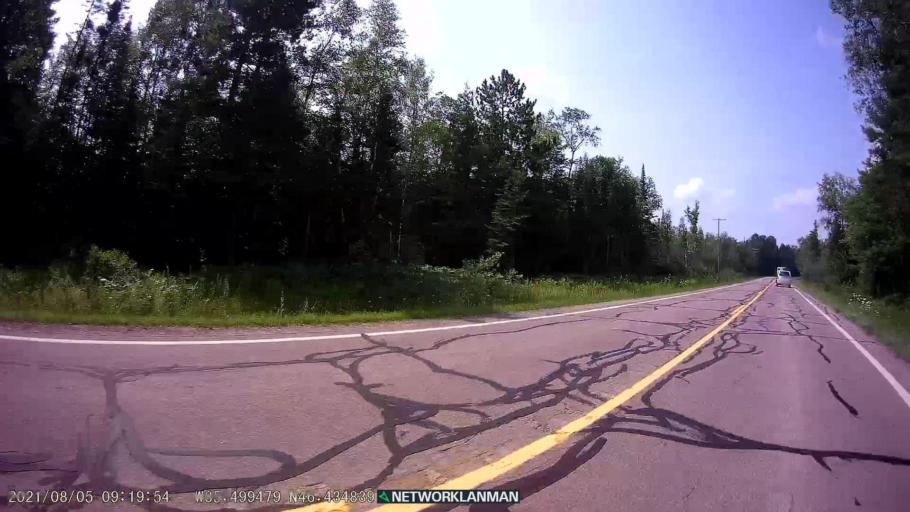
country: US
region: Michigan
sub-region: Luce County
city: Newberry
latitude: 46.4347
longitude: -85.4998
